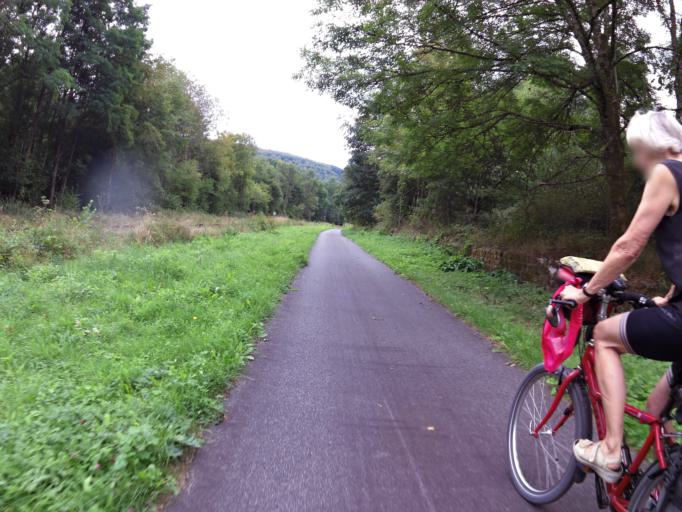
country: DE
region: Rheinland-Pfalz
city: Sankt Thomas
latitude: 50.0785
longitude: 6.6018
